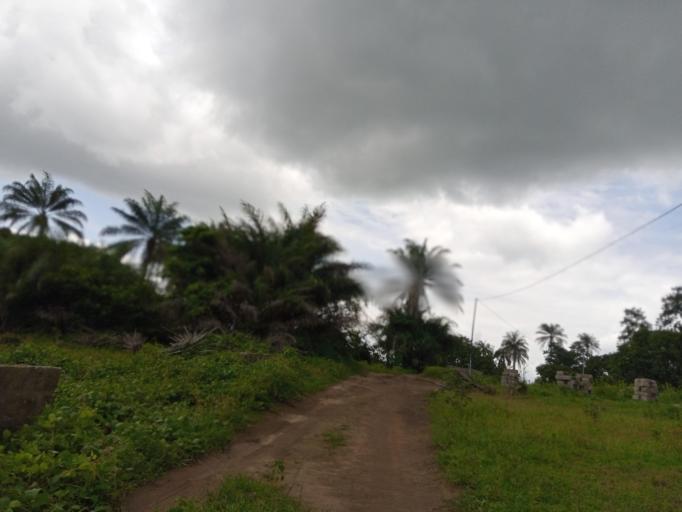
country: SL
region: Northern Province
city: Masoyila
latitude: 8.5857
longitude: -13.1611
